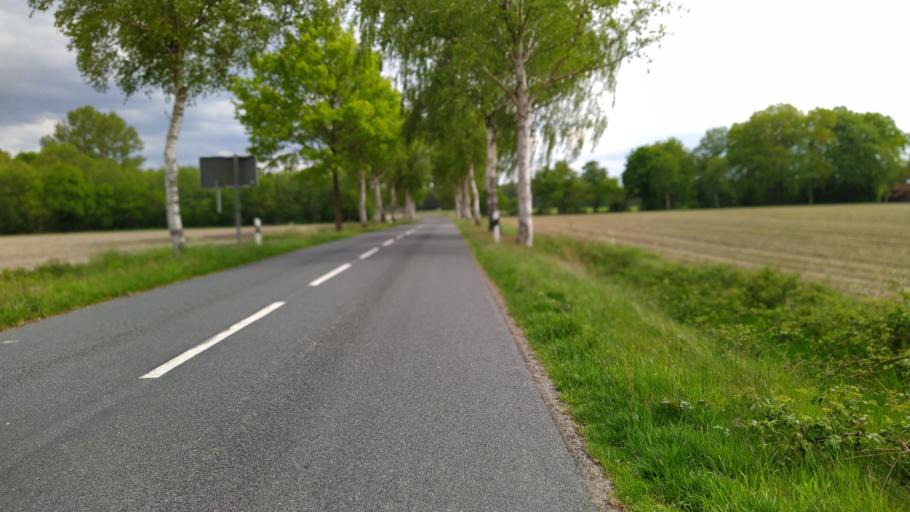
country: DE
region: Lower Saxony
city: Farven
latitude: 53.4409
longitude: 9.3500
